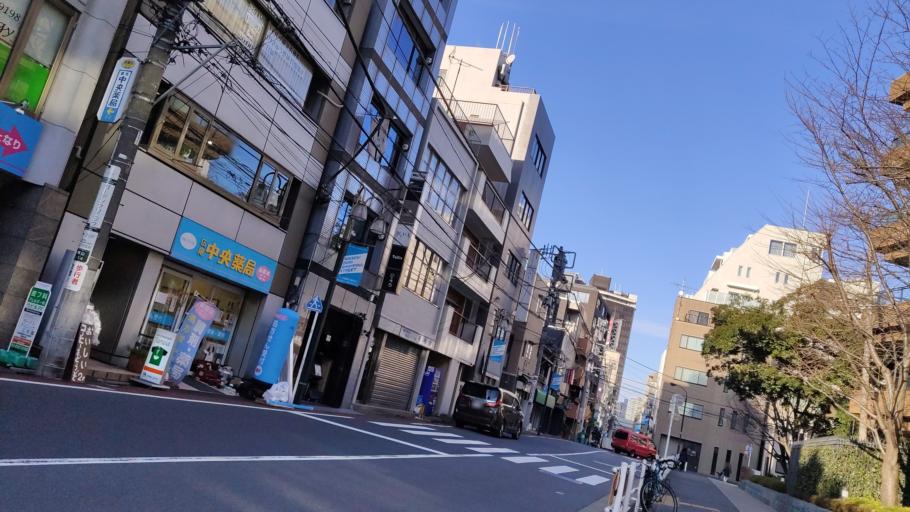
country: JP
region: Tokyo
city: Tokyo
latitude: 35.6565
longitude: 139.7180
